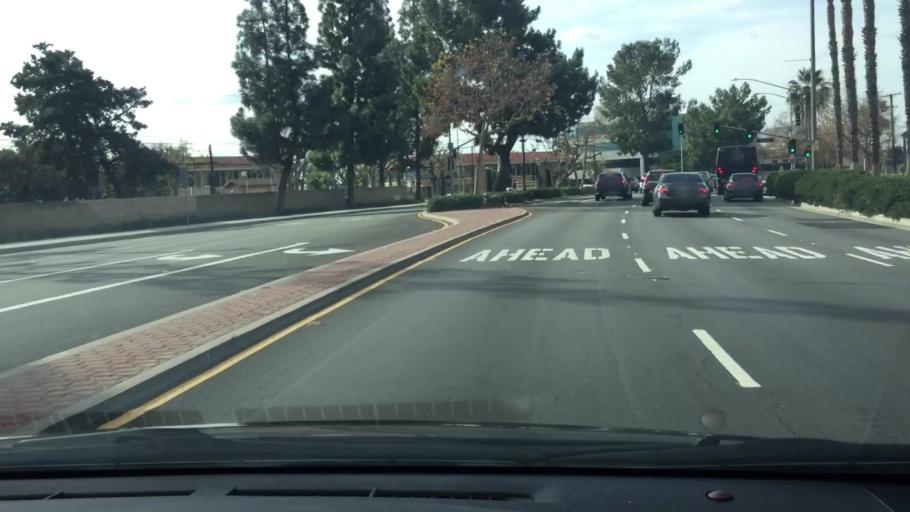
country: US
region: California
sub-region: Orange County
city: Orange
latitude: 33.8068
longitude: -117.8702
